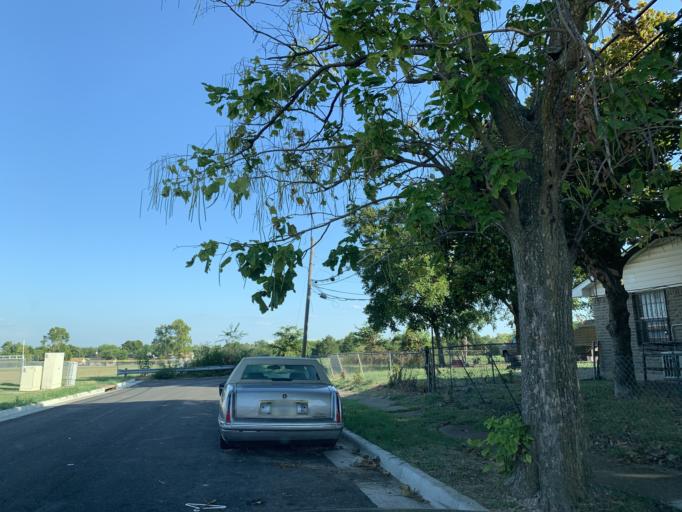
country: US
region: Texas
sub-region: Dallas County
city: Hutchins
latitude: 32.6618
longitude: -96.7606
